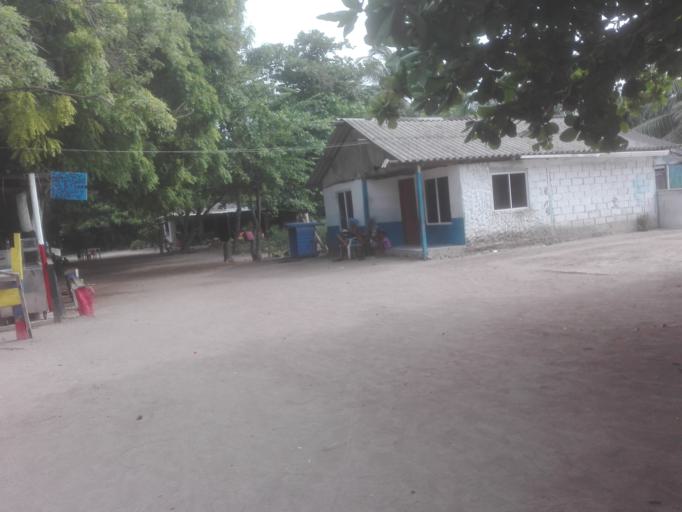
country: CO
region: Bolivar
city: Turbana
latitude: 10.1765
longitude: -75.7421
